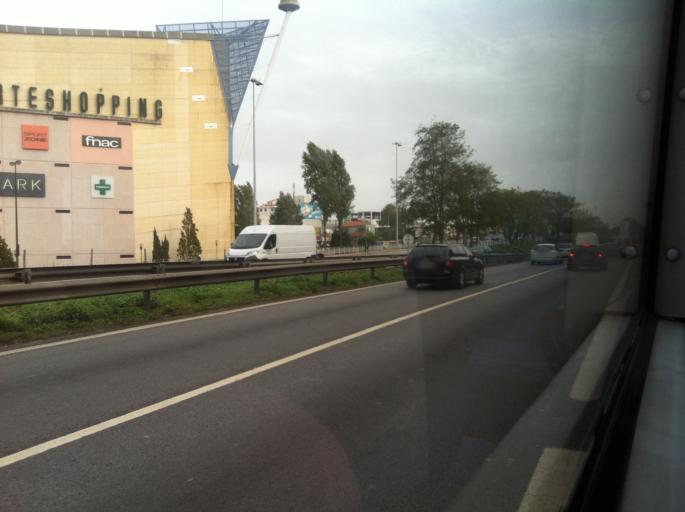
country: PT
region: Porto
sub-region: Matosinhos
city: Senhora da Hora
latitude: 41.1795
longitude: -8.6574
